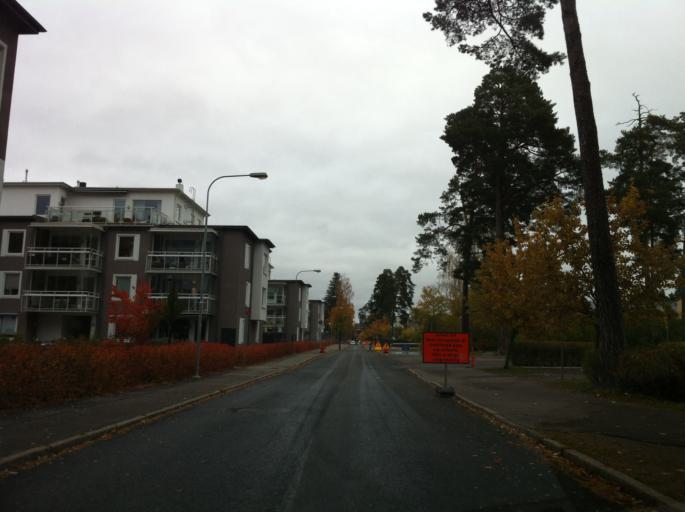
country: SE
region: OEstergoetland
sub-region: Linkopings Kommun
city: Linkoping
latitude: 58.4027
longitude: 15.5952
